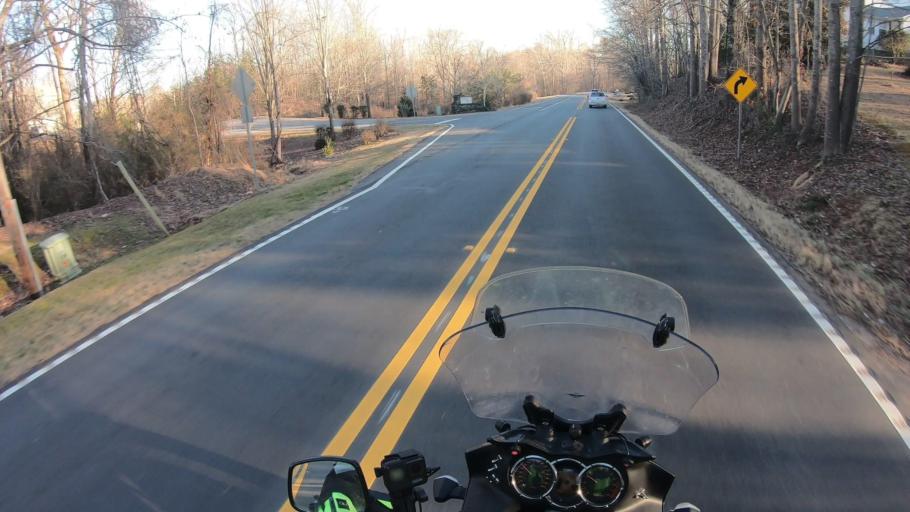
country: US
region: Georgia
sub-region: Lumpkin County
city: Dahlonega
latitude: 34.5789
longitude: -83.9701
